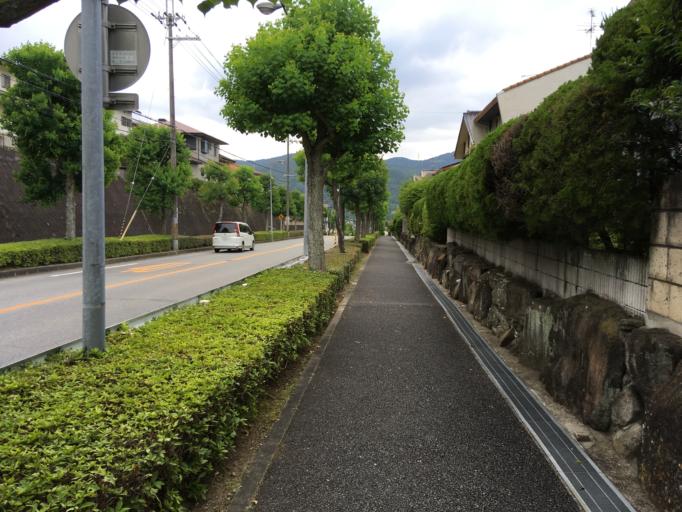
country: JP
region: Nara
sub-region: Ikoma-shi
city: Ikoma
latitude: 34.6568
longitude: 135.7145
